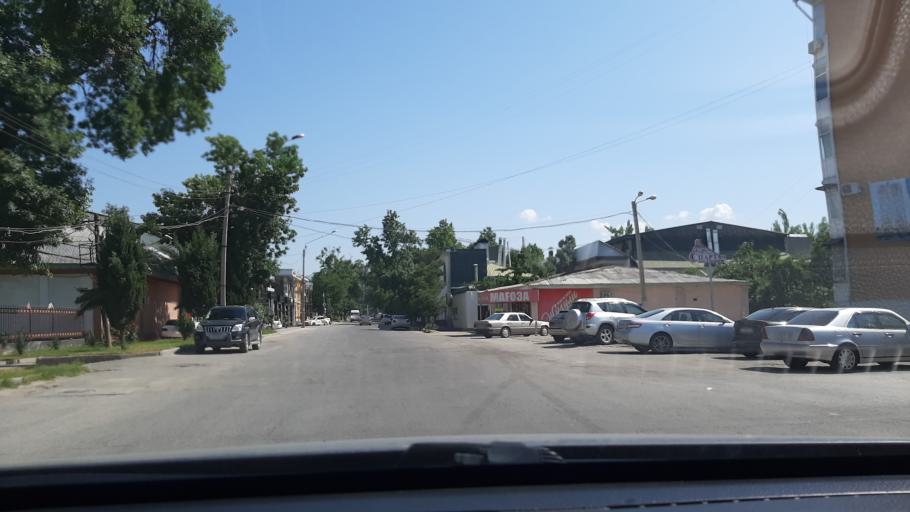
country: TJ
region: Dushanbe
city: Dushanbe
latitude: 38.5556
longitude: 68.7566
